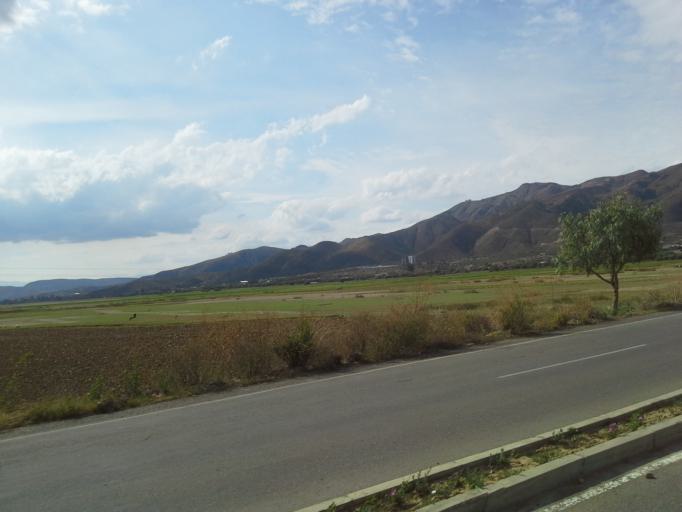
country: BO
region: Cochabamba
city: Tarata
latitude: -17.5562
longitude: -66.0078
